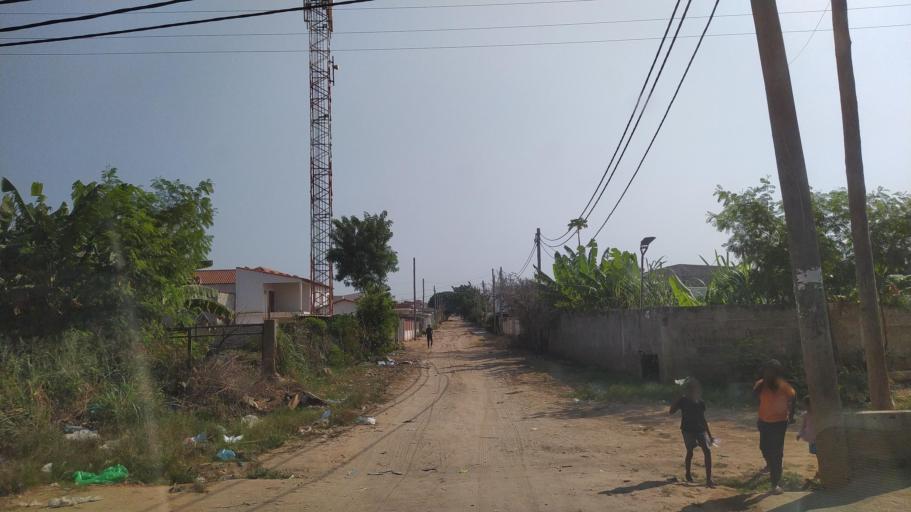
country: AO
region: Luanda
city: Luanda
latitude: -8.9386
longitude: 13.2549
